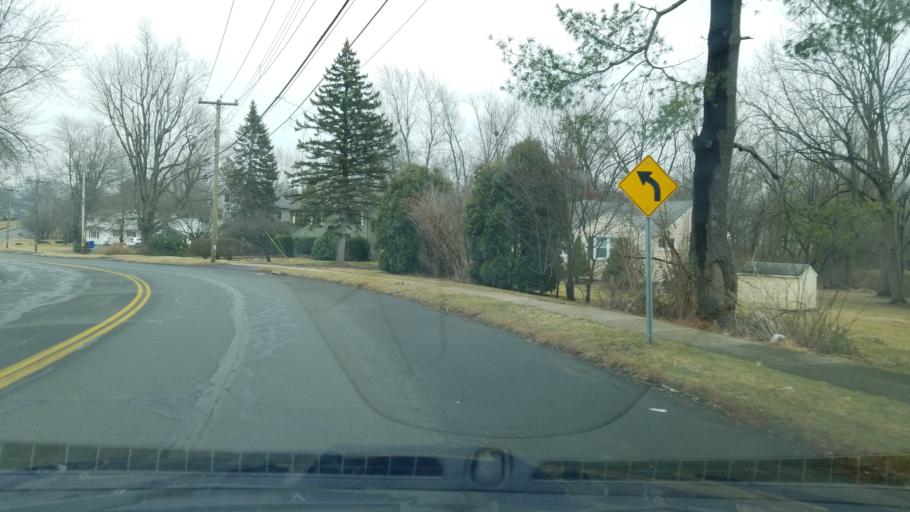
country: US
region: Connecticut
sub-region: Hartford County
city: Wethersfield
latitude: 41.6834
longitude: -72.6722
